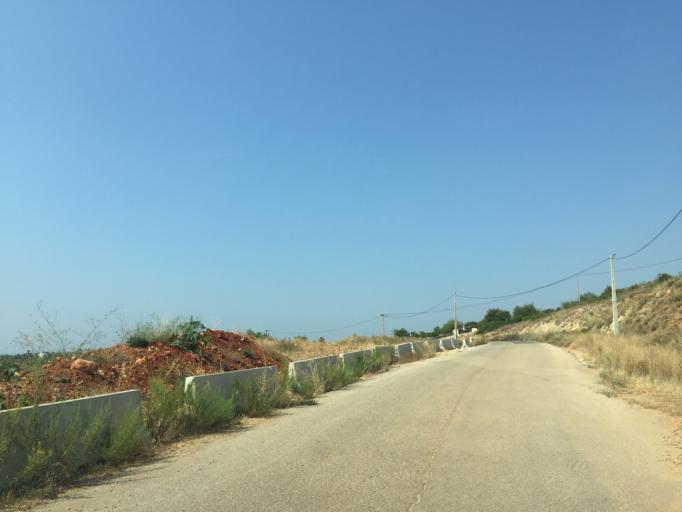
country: PT
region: Faro
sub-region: Loule
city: Almancil
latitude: 37.1007
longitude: -8.0061
